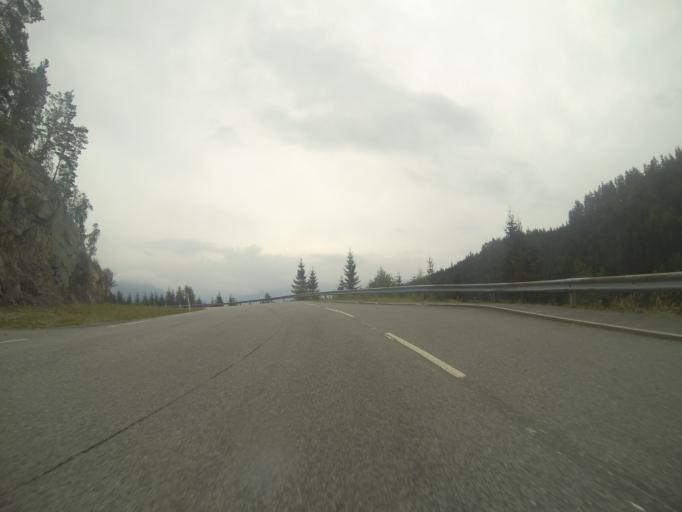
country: NO
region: Rogaland
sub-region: Suldal
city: Sand
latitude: 59.5093
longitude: 6.2099
